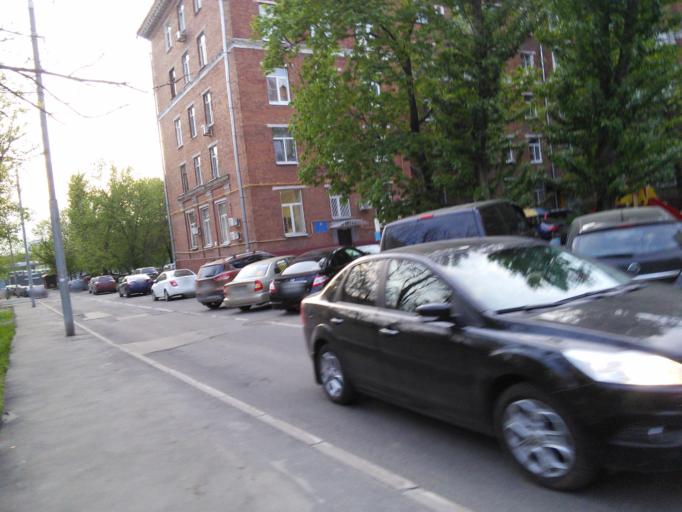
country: RU
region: Moscow
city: Mar'ina Roshcha
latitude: 55.8057
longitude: 37.6120
